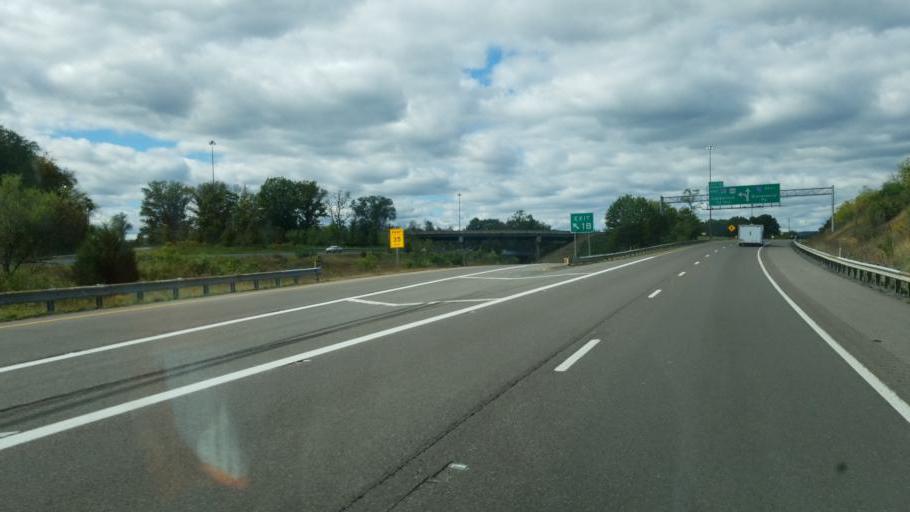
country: US
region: Maryland
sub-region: Washington County
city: Hancock
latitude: 39.7069
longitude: -78.1811
